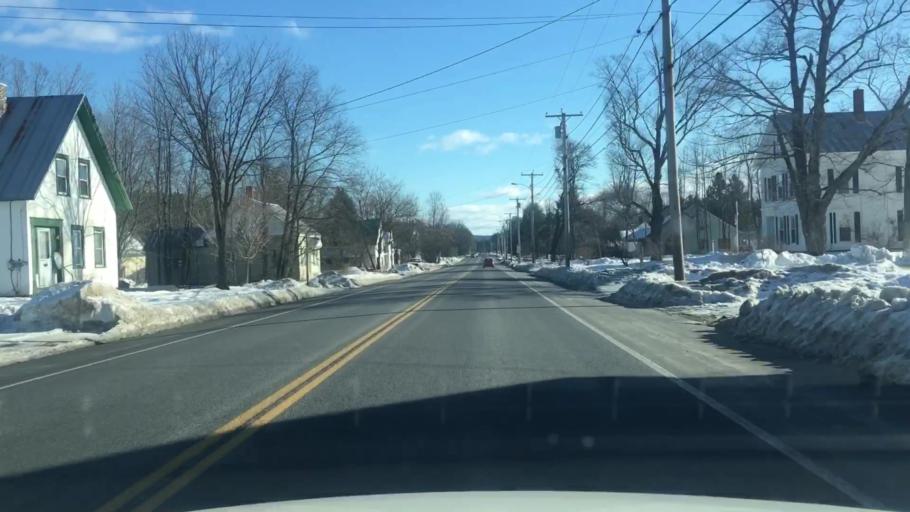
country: US
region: Maine
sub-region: Somerset County
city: Madison
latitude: 44.9479
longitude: -69.8571
